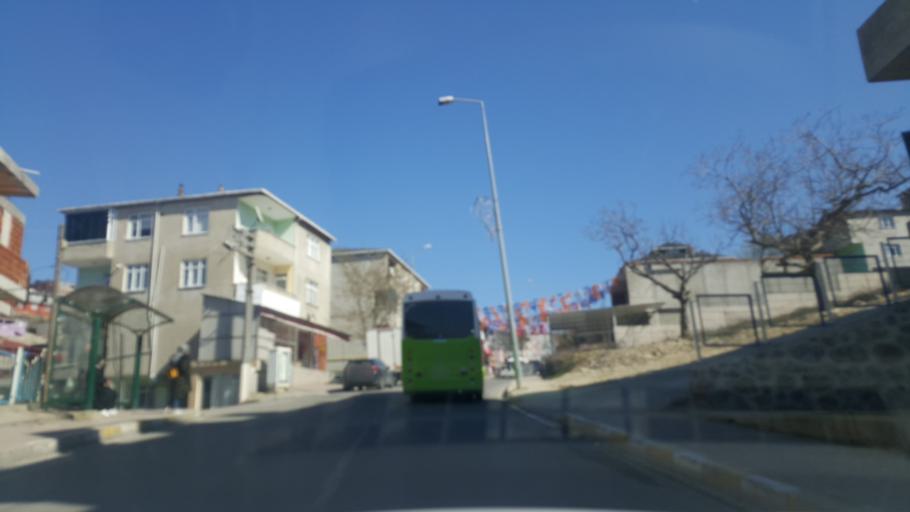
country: TR
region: Kocaeli
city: Tavsancil
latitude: 40.7856
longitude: 29.5530
